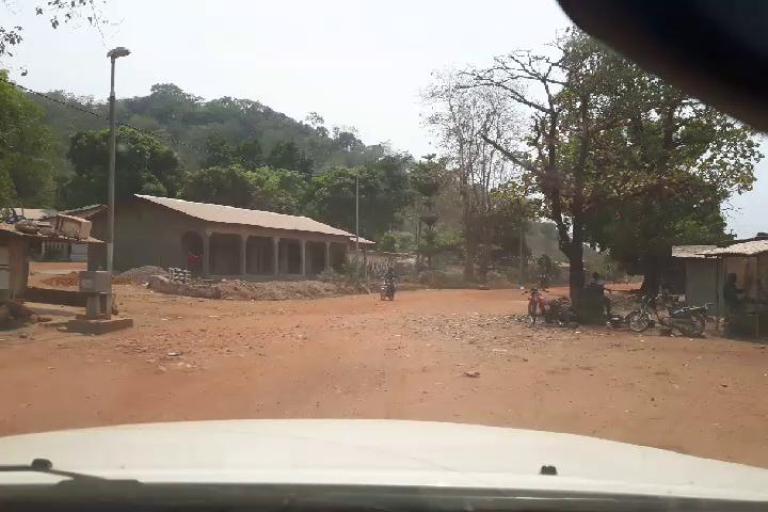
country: SL
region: Northern Province
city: Bumbuna
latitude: 9.0439
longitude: -11.7515
